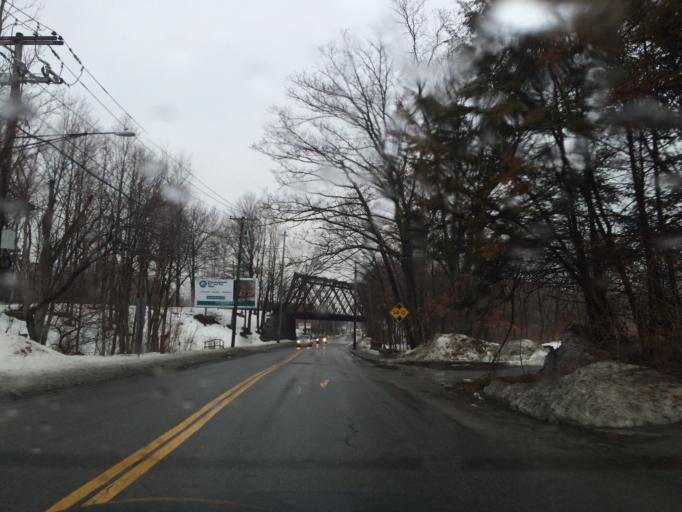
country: US
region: Massachusetts
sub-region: Middlesex County
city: Waltham
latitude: 42.3810
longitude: -71.2192
